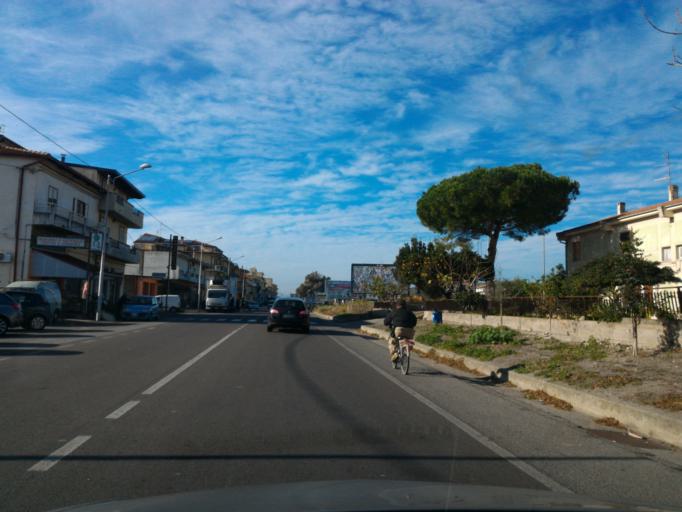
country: IT
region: Calabria
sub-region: Provincia di Catanzaro
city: Botricello
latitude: 38.9334
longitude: 16.8502
